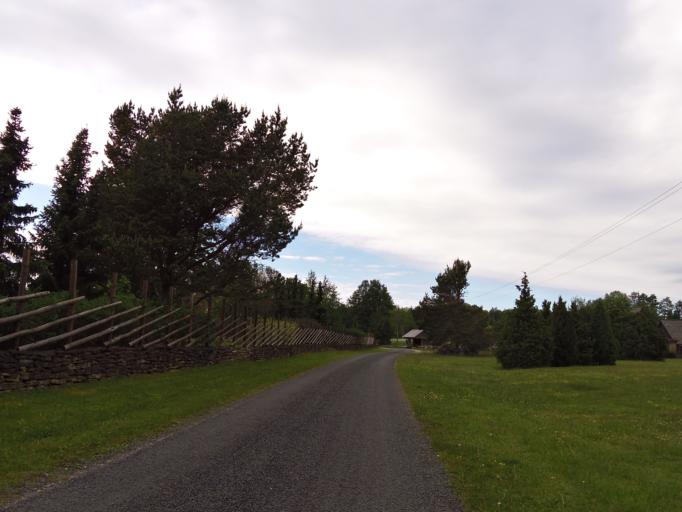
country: EE
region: Harju
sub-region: Paldiski linn
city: Paldiski
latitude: 59.2551
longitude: 23.7487
